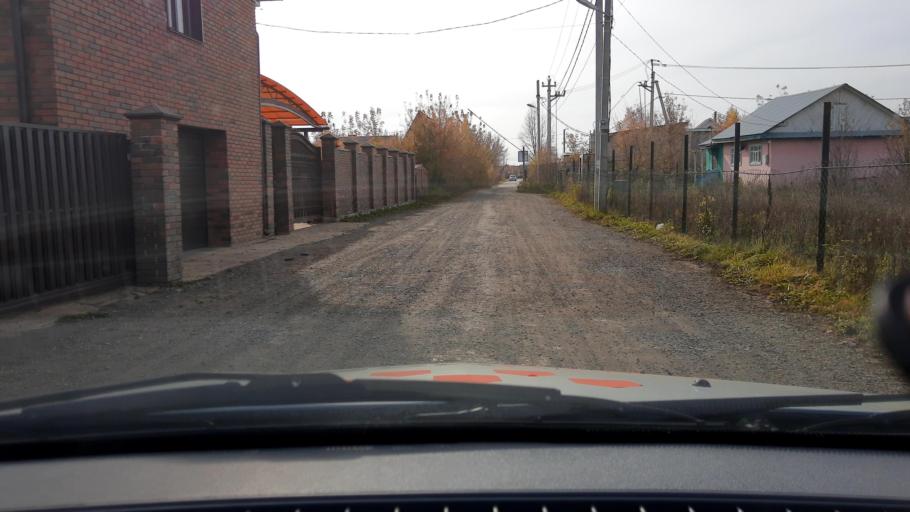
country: RU
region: Bashkortostan
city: Mikhaylovka
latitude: 54.7902
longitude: 55.8318
